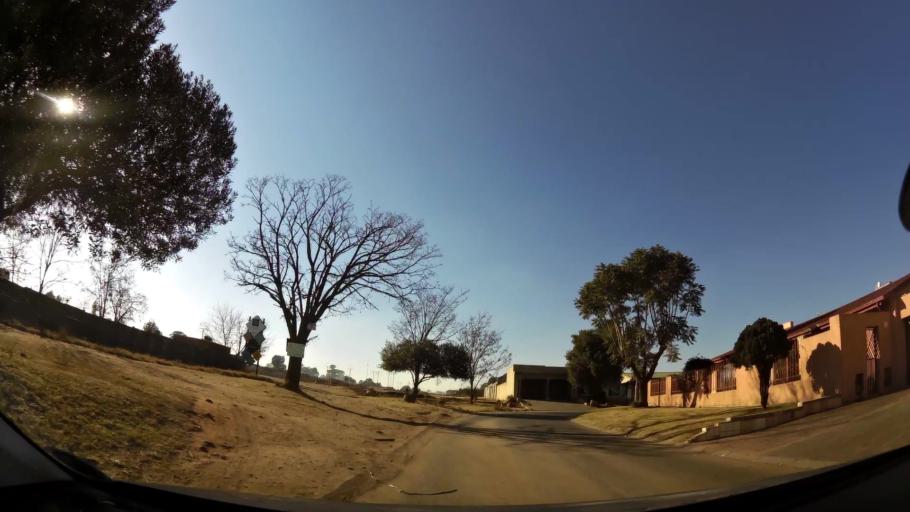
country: ZA
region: Gauteng
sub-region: City of Johannesburg Metropolitan Municipality
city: Johannesburg
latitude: -26.2036
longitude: 27.9603
